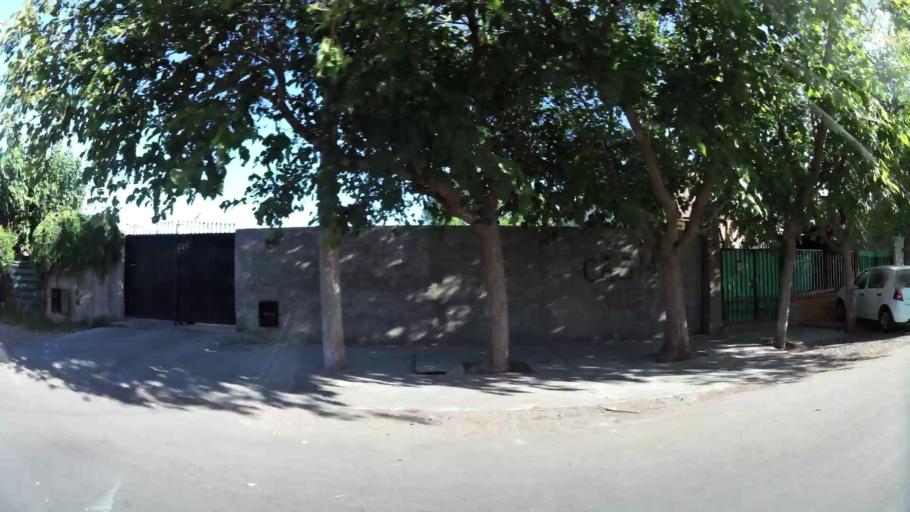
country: AR
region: San Juan
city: Villa Krause
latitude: -31.5646
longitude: -68.5205
